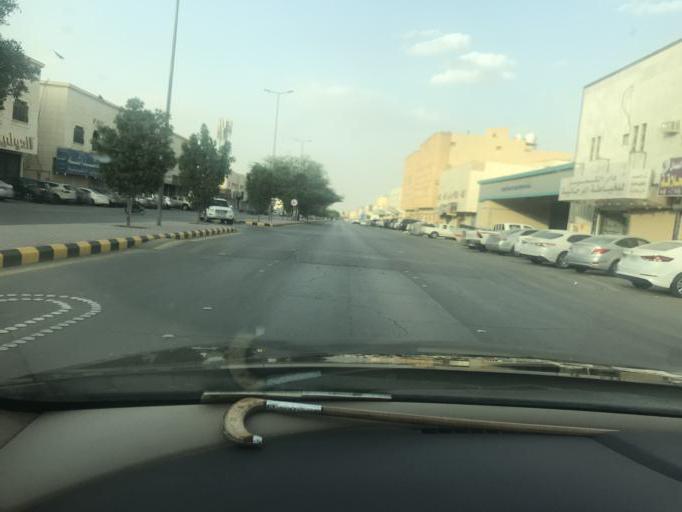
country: SA
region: Ar Riyad
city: Riyadh
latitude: 24.7332
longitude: 46.7683
